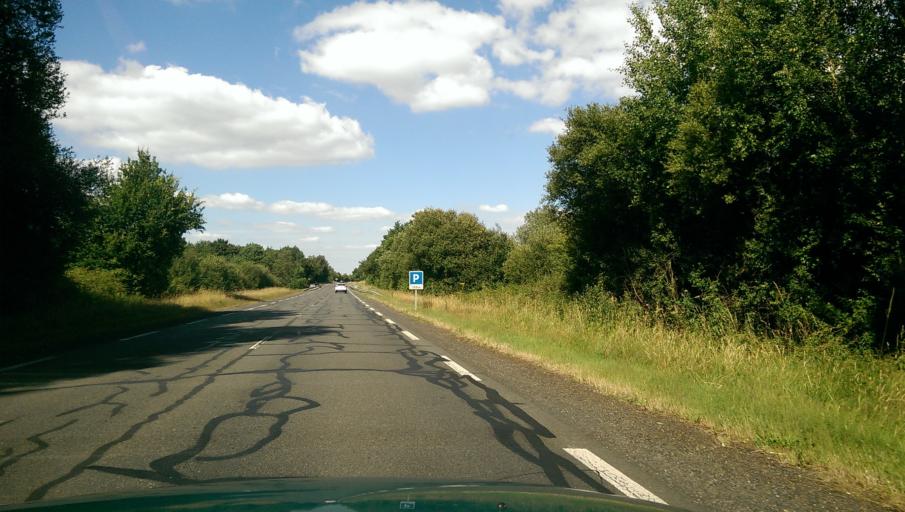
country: FR
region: Pays de la Loire
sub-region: Departement de la Loire-Atlantique
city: Lege
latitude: 46.8868
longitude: -1.6120
